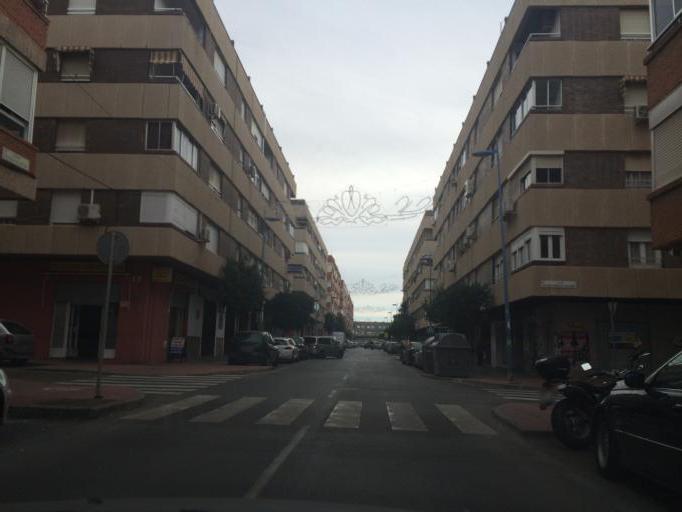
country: ES
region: Andalusia
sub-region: Provincia de Almeria
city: Almeria
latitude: 36.8382
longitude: -2.4506
